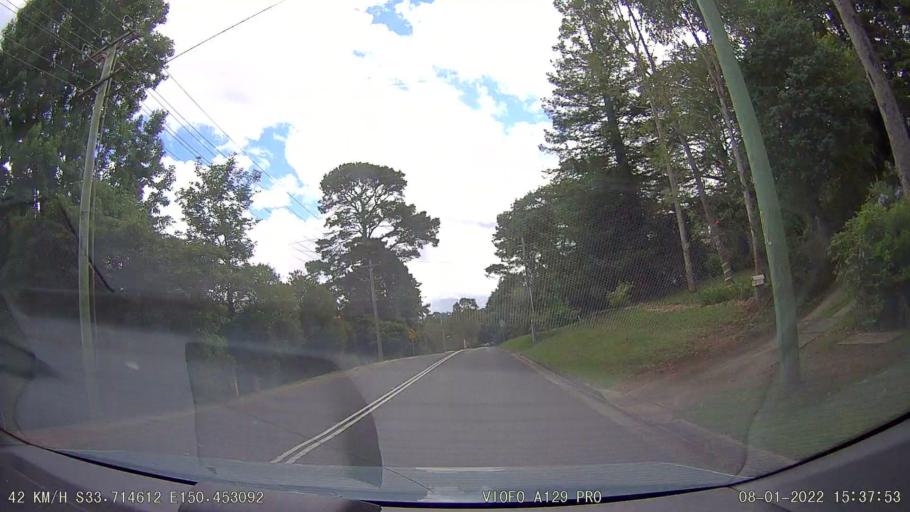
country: AU
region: New South Wales
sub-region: Blue Mountains Municipality
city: Hazelbrook
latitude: -33.7144
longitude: 150.4532
